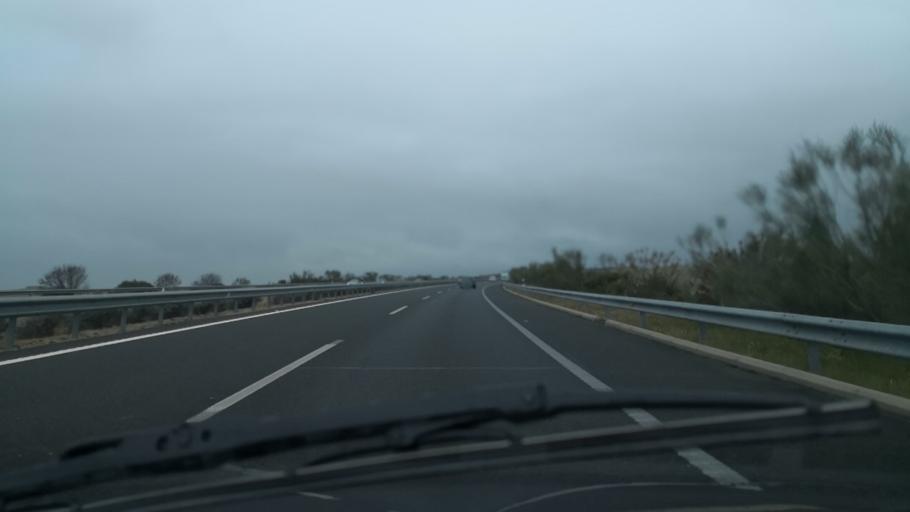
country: ES
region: Extremadura
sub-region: Provincia de Caceres
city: Casar de Caceres
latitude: 39.5737
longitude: -6.4022
